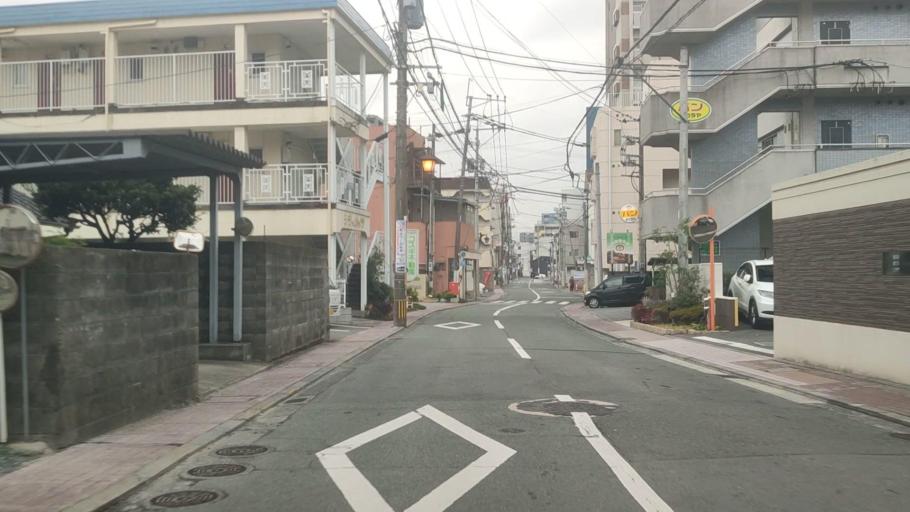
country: JP
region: Kumamoto
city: Kumamoto
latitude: 32.7964
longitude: 130.7169
